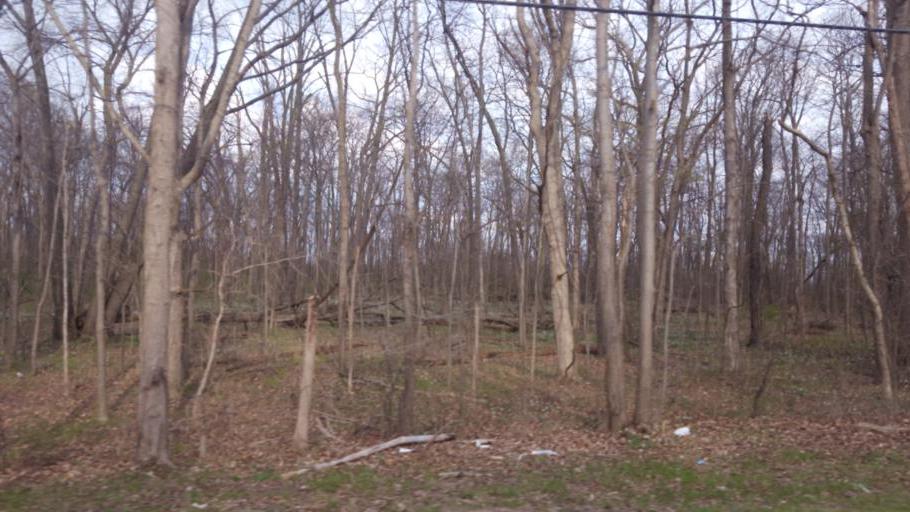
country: US
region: Ohio
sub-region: Erie County
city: Sandusky
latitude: 41.5121
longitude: -82.7618
